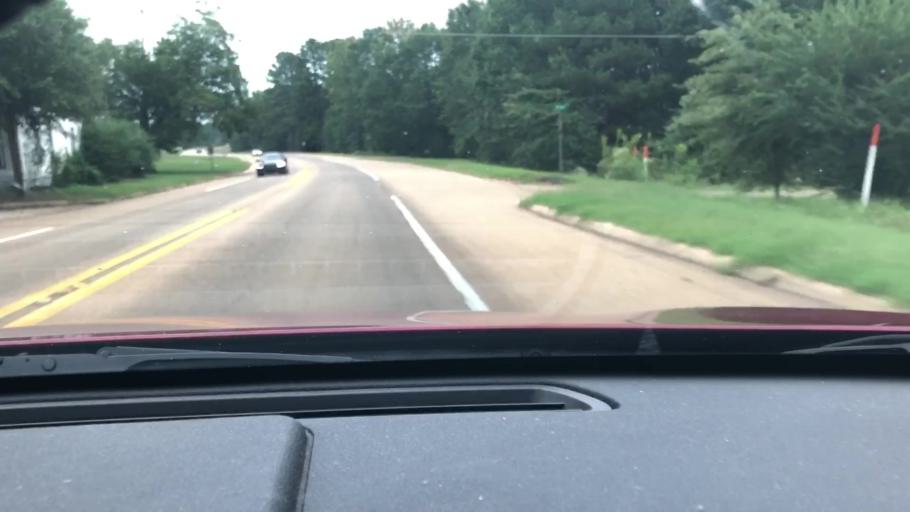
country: US
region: Arkansas
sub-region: Lafayette County
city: Stamps
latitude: 33.3584
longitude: -93.4339
